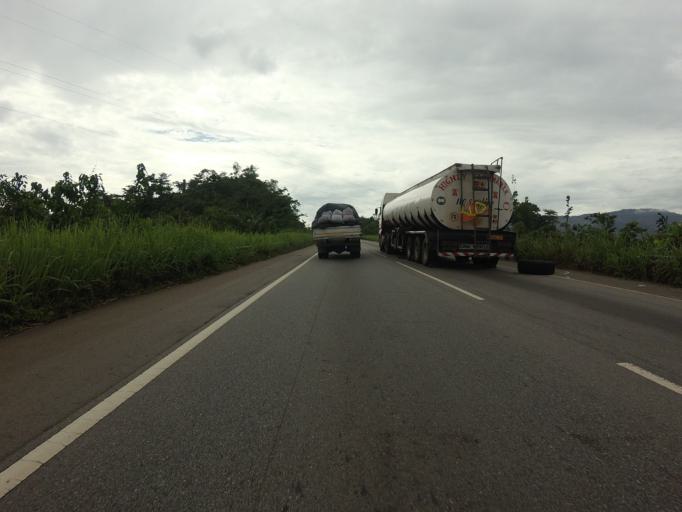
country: GH
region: Eastern
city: Nkawkaw
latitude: 6.5530
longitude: -0.7952
